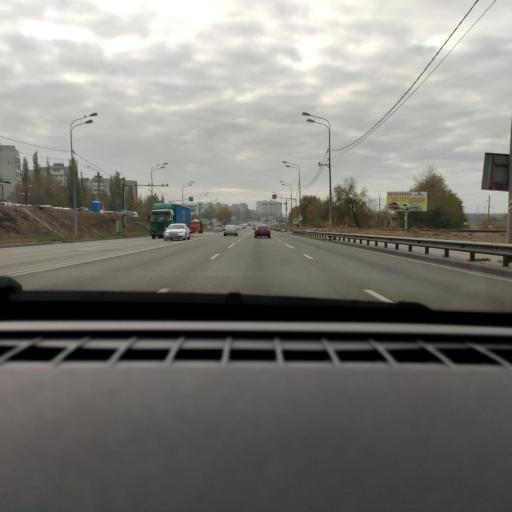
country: RU
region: Voronezj
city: Podgornoye
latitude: 51.7075
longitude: 39.1363
